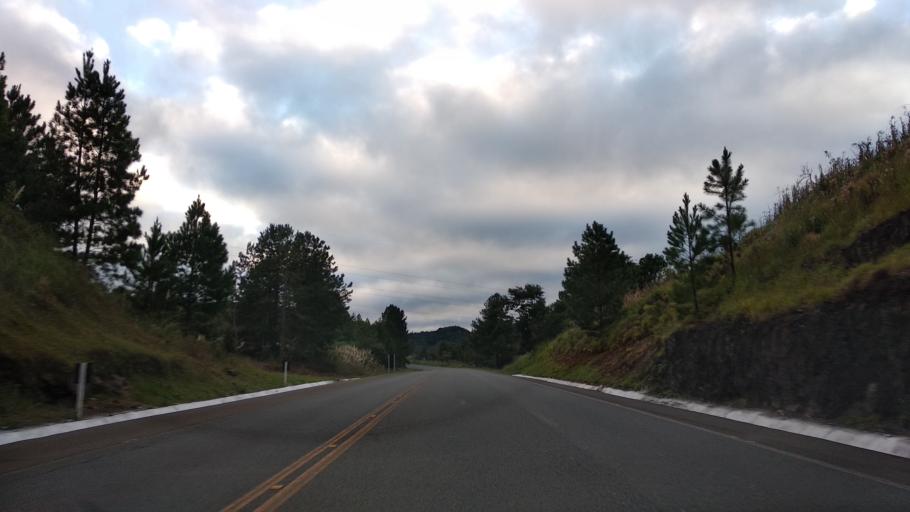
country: BR
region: Santa Catarina
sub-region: Campos Novos
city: Campos Novos
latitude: -27.5009
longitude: -50.9494
